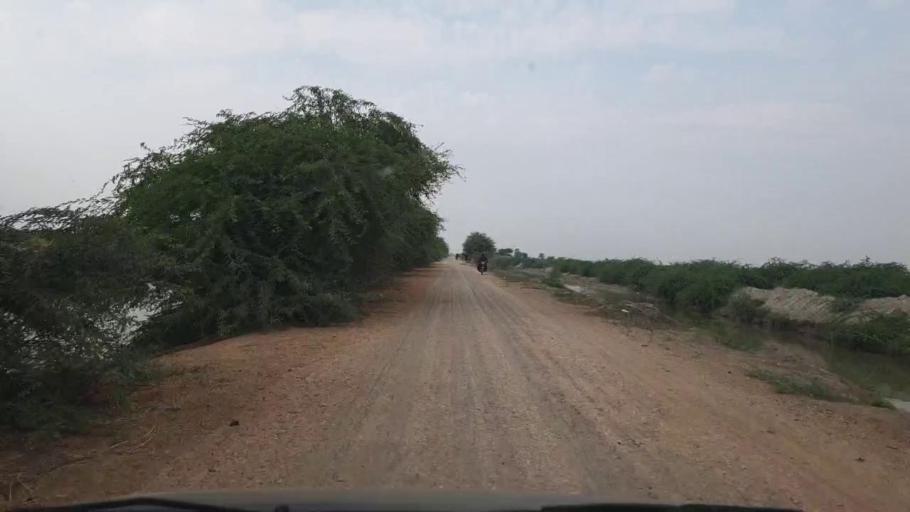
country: PK
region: Sindh
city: Kario
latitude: 24.6064
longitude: 68.5968
